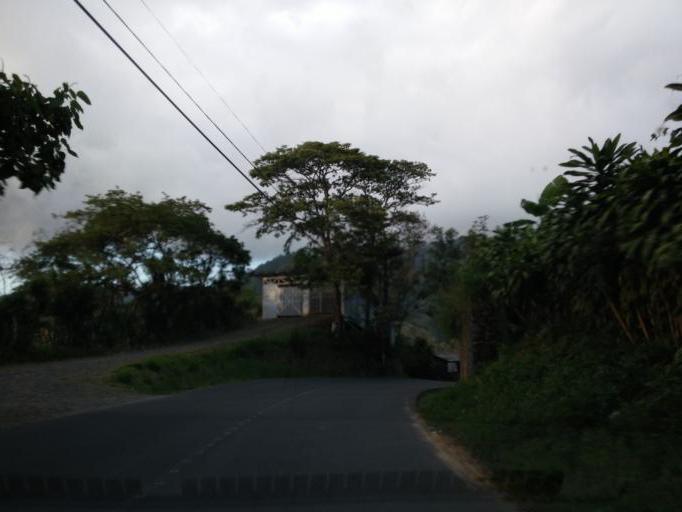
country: CR
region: San Jose
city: Palmichal
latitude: 9.8354
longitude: -84.2088
